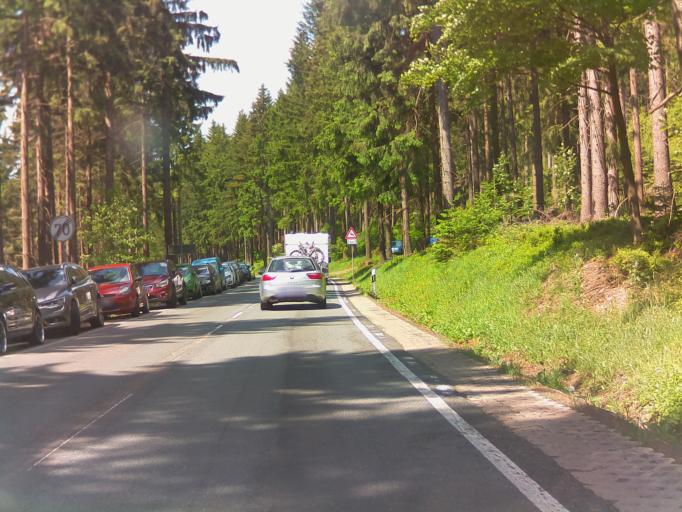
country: DE
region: Thuringia
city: Tambach-Dietharz
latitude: 50.7708
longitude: 10.5641
